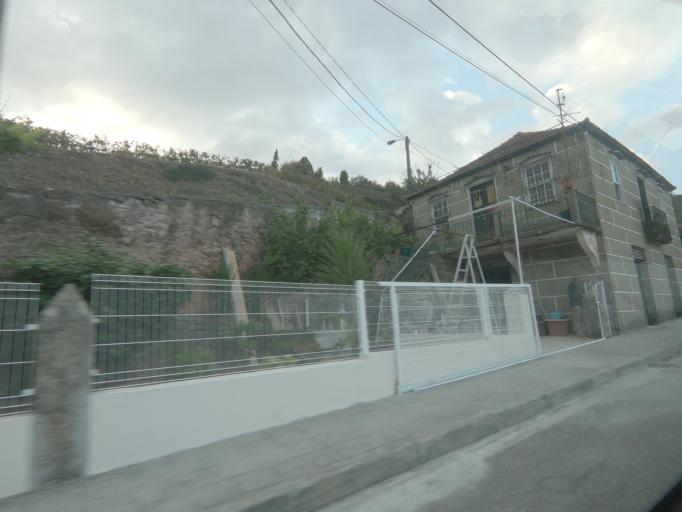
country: PT
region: Vila Real
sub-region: Mesao Frio
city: Mesao Frio
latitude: 41.1747
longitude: -7.8652
